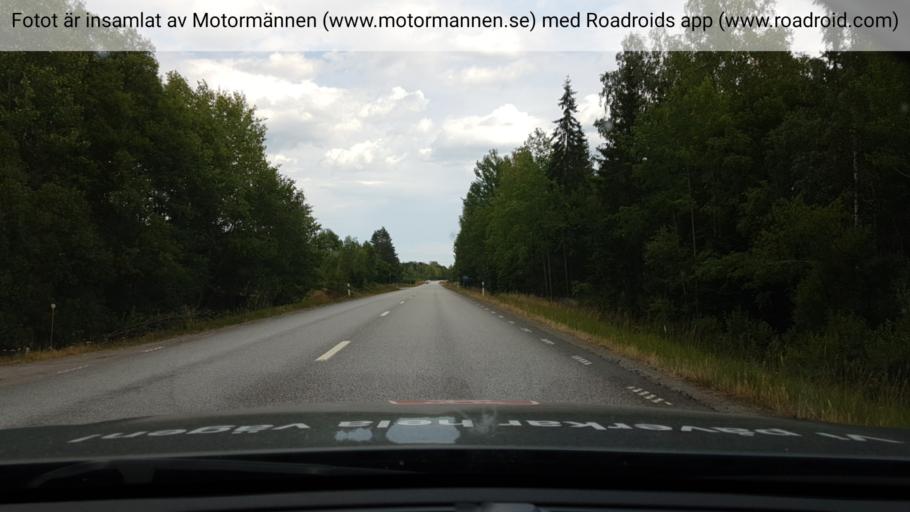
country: SE
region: Uppsala
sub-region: Heby Kommun
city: Morgongava
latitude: 59.8923
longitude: 17.1584
